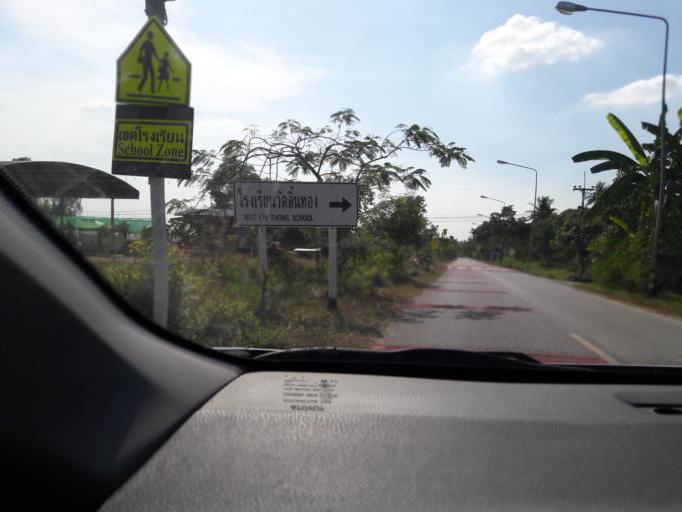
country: TH
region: Ang Thong
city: Wiset Chaichan
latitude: 14.5728
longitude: 100.3922
